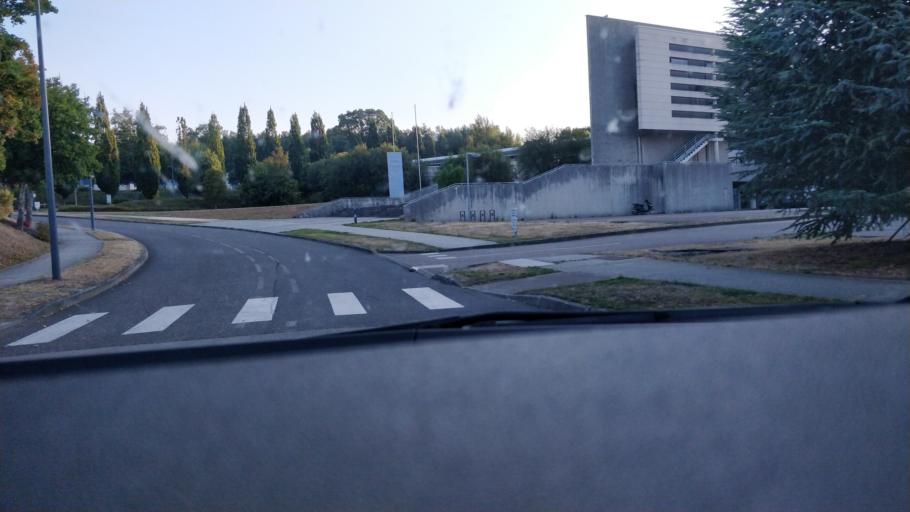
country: FR
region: Limousin
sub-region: Departement de la Haute-Vienne
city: Le Palais-sur-Vienne
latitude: 45.8606
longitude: 1.2942
